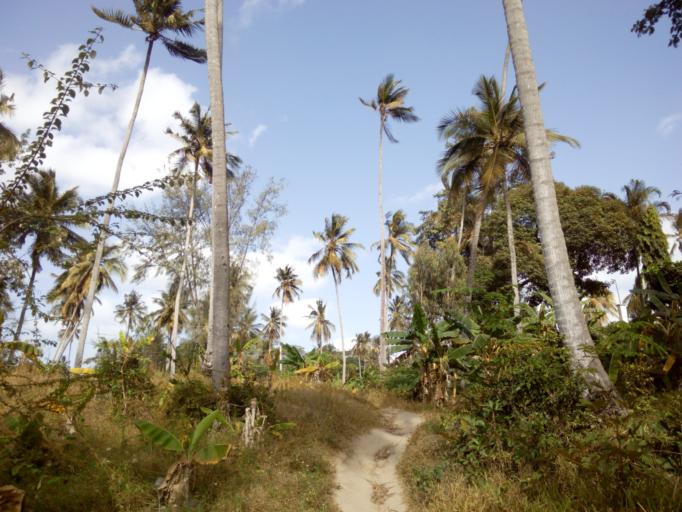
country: TZ
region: Zanzibar Urban/West
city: Zanzibar
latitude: -6.1808
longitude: 39.2021
